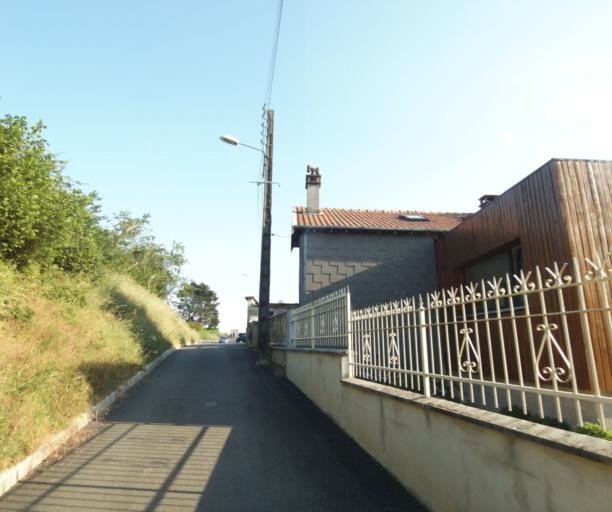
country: FR
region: Champagne-Ardenne
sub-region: Departement des Ardennes
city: Charleville-Mezieres
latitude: 49.7905
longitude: 4.7094
